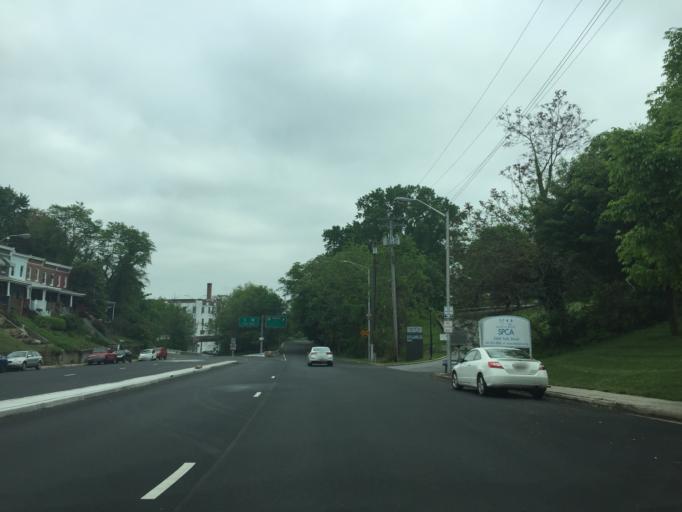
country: US
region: Maryland
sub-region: City of Baltimore
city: Baltimore
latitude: 39.3287
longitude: -76.6343
